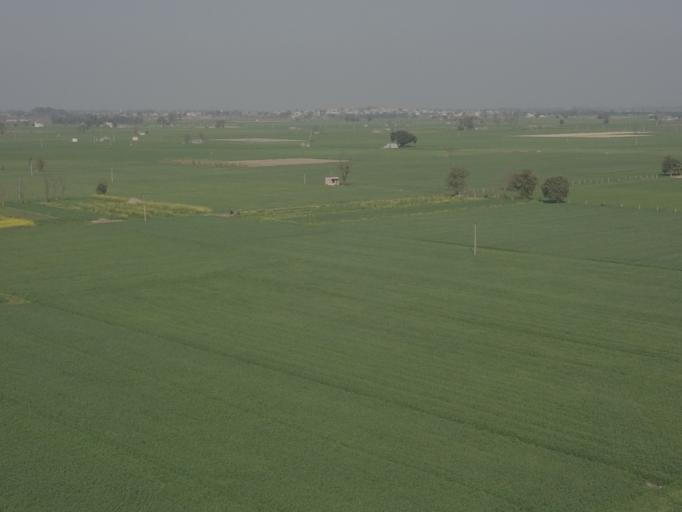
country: IN
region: Punjab
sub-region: Shahid Bhagat Singh Nagar
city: Rahon
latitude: 31.0236
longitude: 76.0890
